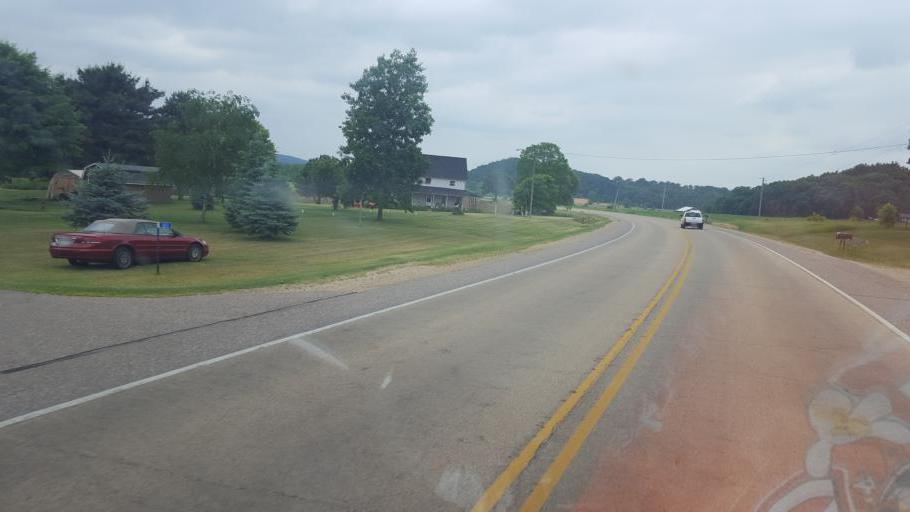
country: US
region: Wisconsin
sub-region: Sauk County
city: Reedsburg
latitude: 43.6156
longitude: -90.1415
